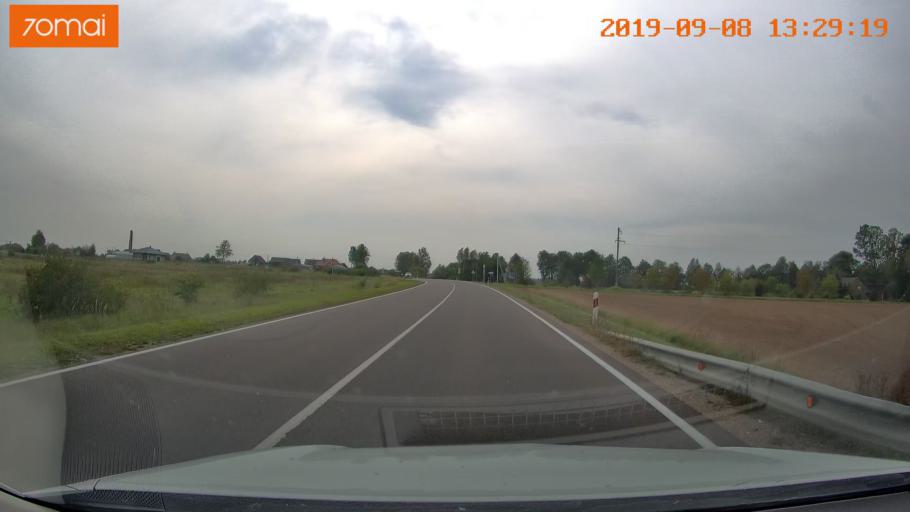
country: LT
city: Jieznas
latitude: 54.5643
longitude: 24.1635
